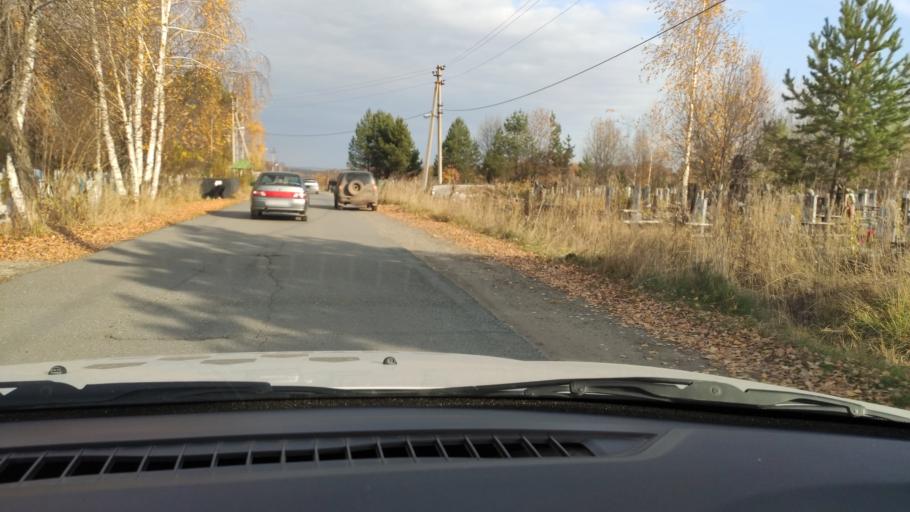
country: RU
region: Perm
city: Kondratovo
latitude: 58.0647
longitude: 56.1439
